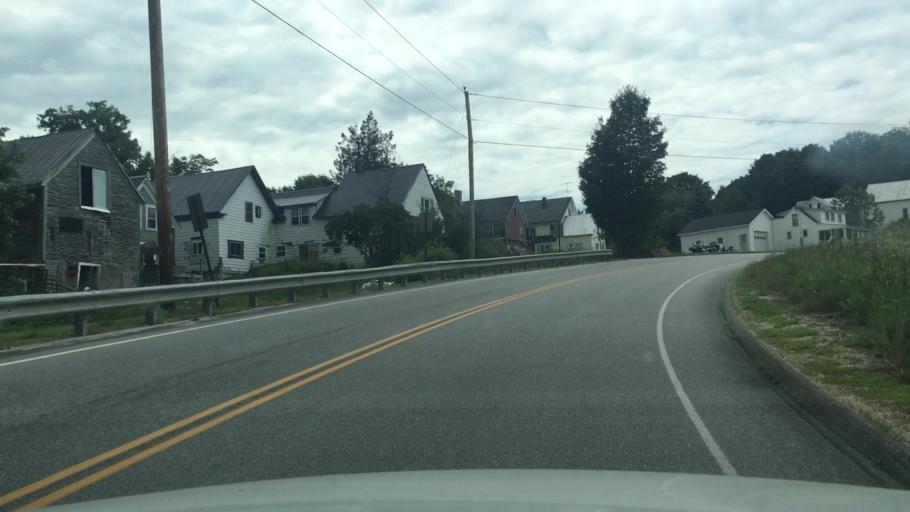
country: US
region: Maine
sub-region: Oxford County
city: Hartford
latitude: 44.3647
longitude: -70.4570
